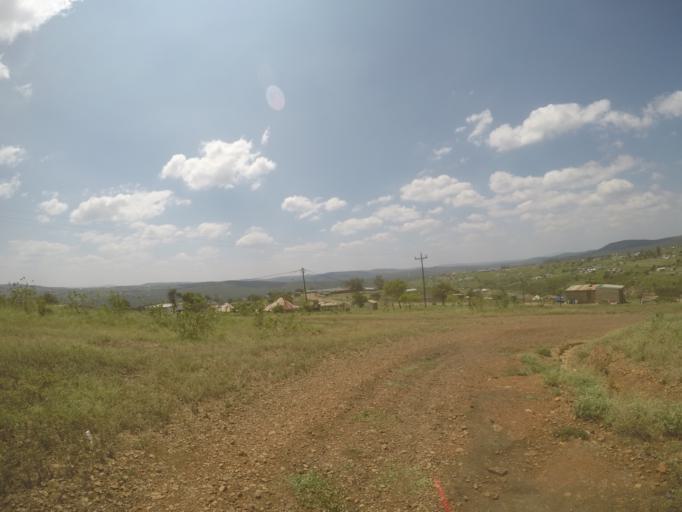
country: ZA
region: KwaZulu-Natal
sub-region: uThungulu District Municipality
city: Empangeni
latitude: -28.5989
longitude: 31.7412
